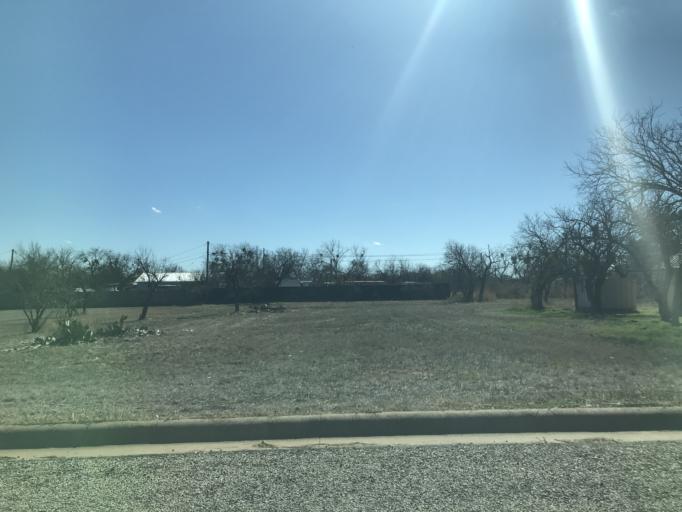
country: US
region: Texas
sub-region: Tom Green County
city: San Angelo
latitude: 31.4644
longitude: -100.4105
